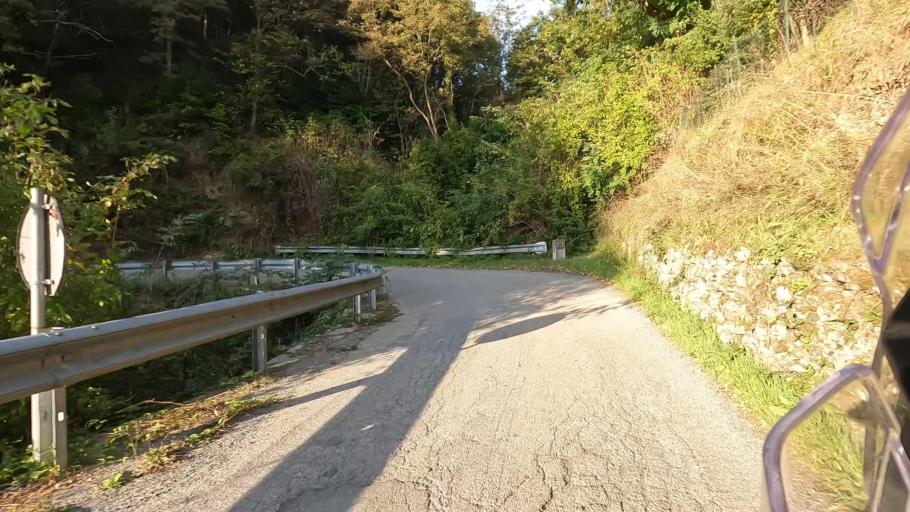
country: IT
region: Liguria
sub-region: Provincia di Savona
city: San Giovanni
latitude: 44.3946
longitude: 8.5245
